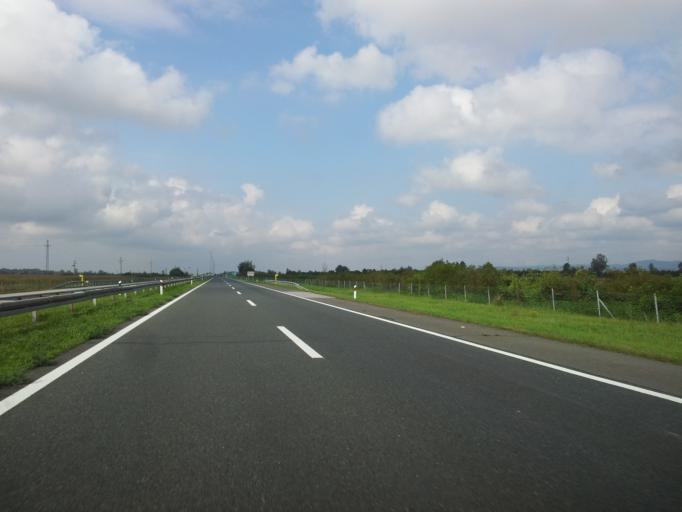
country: HR
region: Brodsko-Posavska
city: Ljupina
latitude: 45.2317
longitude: 17.3044
